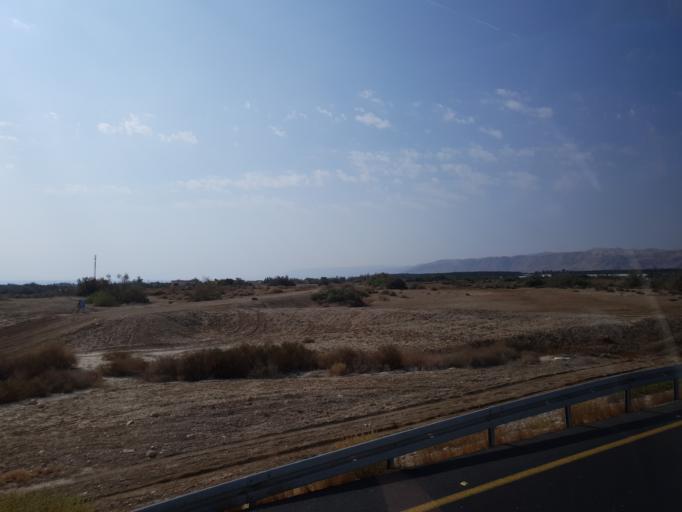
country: PS
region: West Bank
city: Jericho
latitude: 31.7729
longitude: 35.5018
